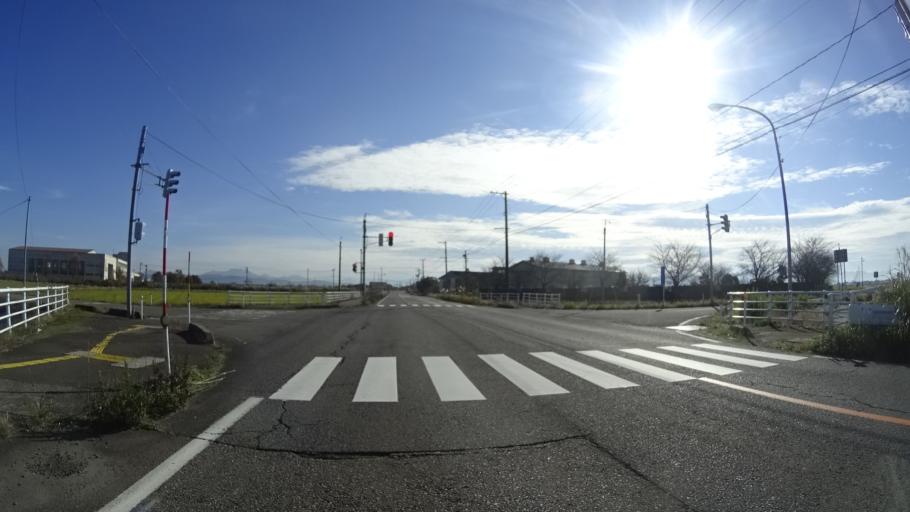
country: JP
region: Niigata
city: Mitsuke
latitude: 37.5536
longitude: 138.8599
